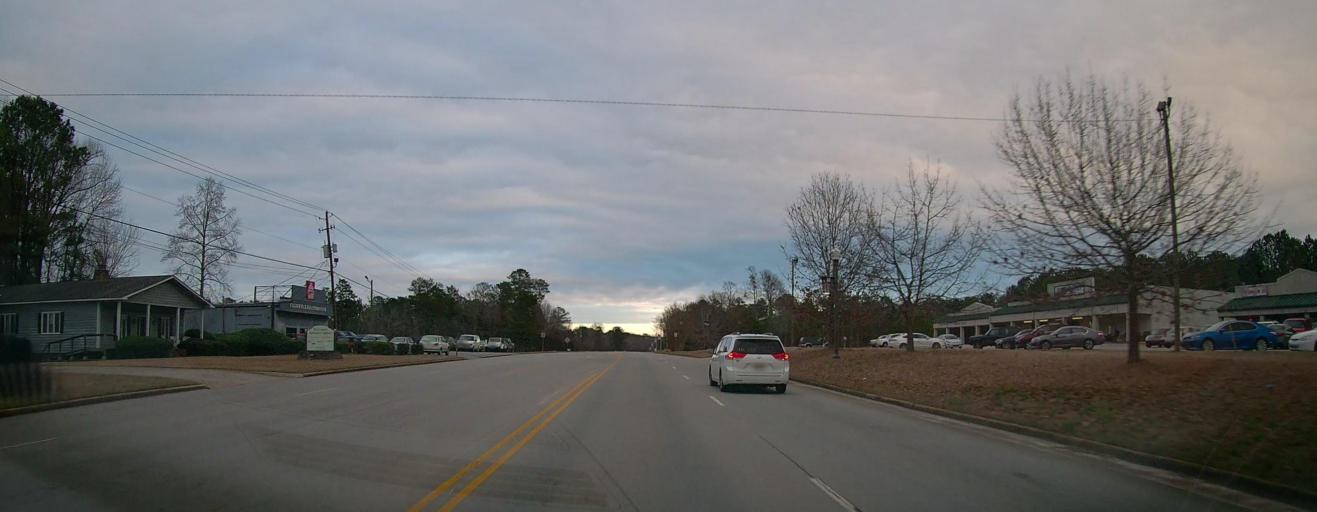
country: US
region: Alabama
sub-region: Chambers County
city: Valley
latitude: 32.8175
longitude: -85.1977
